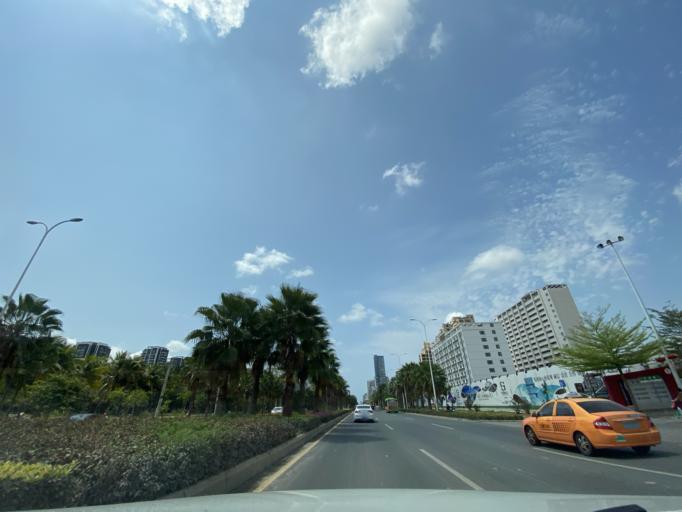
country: CN
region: Hainan
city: Sanya
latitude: 18.2819
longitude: 109.5146
